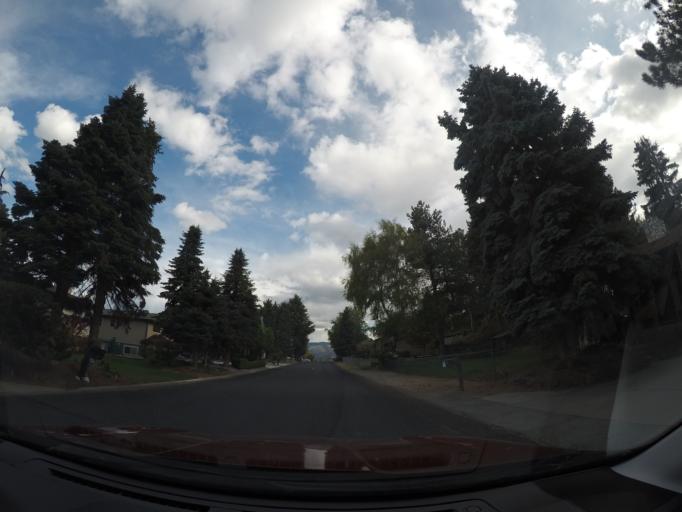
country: US
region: Washington
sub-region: Chelan County
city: Sunnyslope
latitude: 47.4572
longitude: -120.3428
